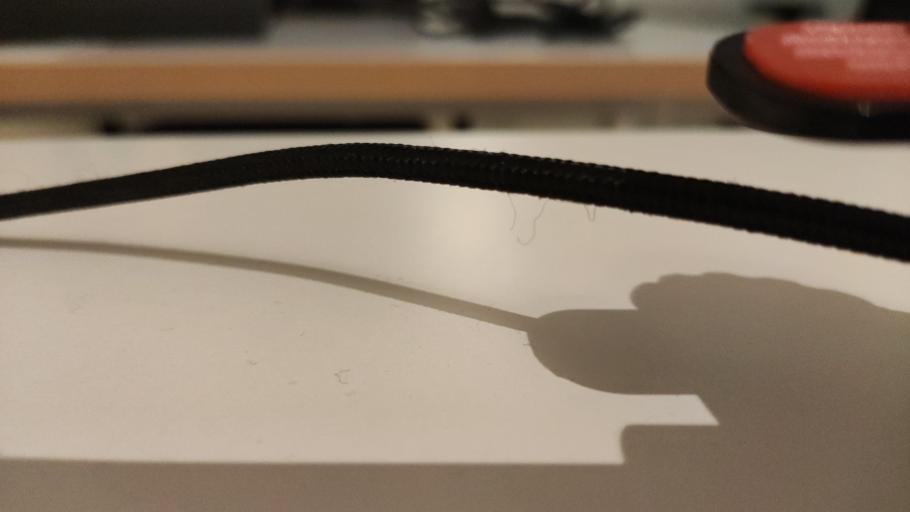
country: RU
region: Moskovskaya
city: Malino
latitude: 55.1111
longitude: 38.1549
